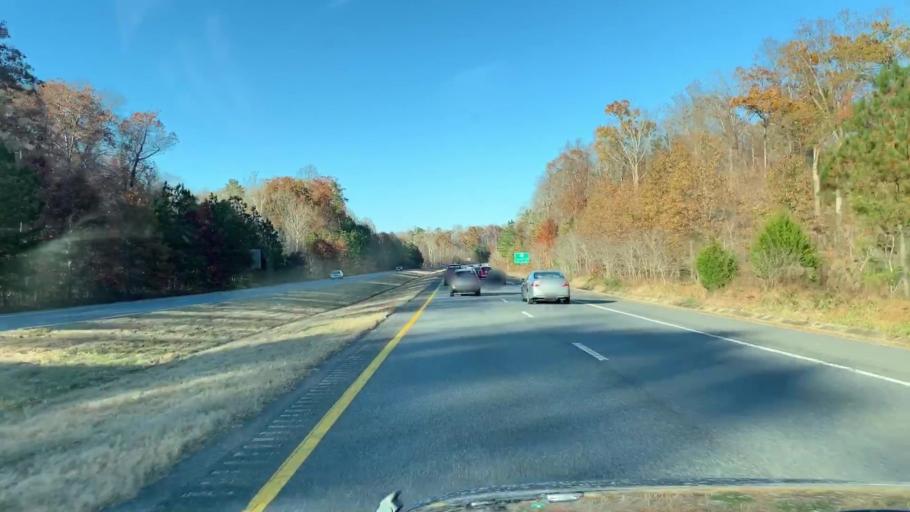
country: US
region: Virginia
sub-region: James City County
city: Williamsburg
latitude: 37.2869
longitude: -76.7529
